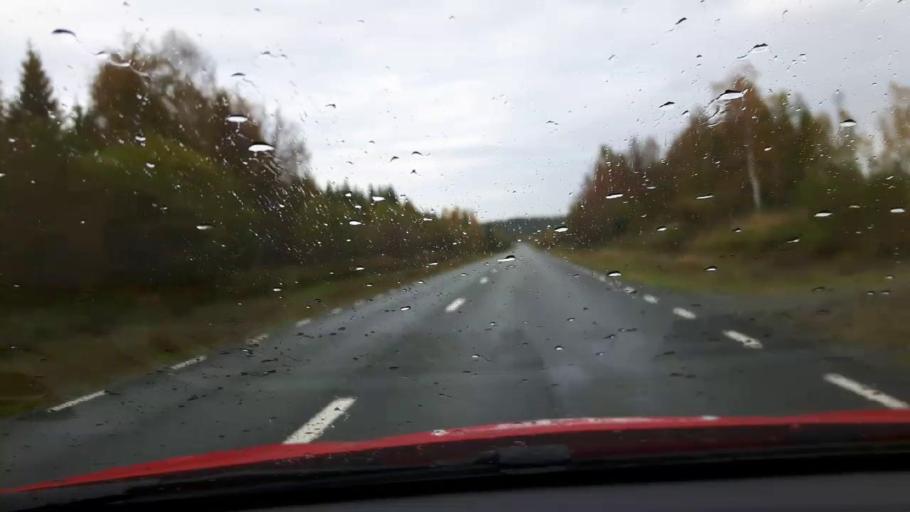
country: SE
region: Jaemtland
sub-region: Krokoms Kommun
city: Krokom
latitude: 63.0863
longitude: 14.2964
